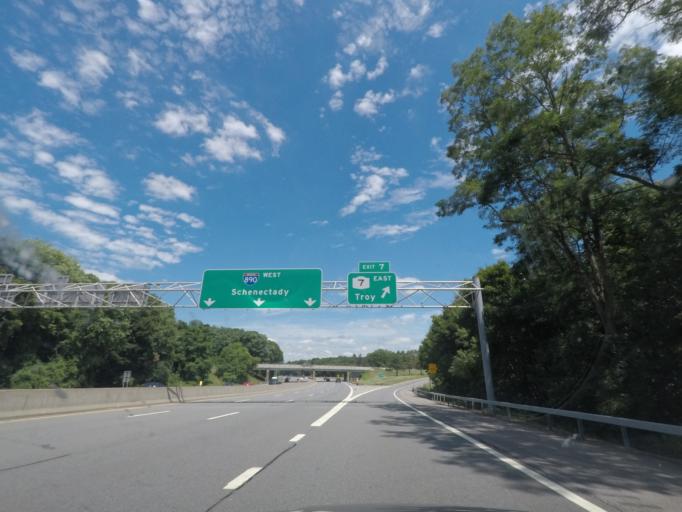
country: US
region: New York
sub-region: Schenectady County
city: Schenectady
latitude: 42.7805
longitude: -73.9234
